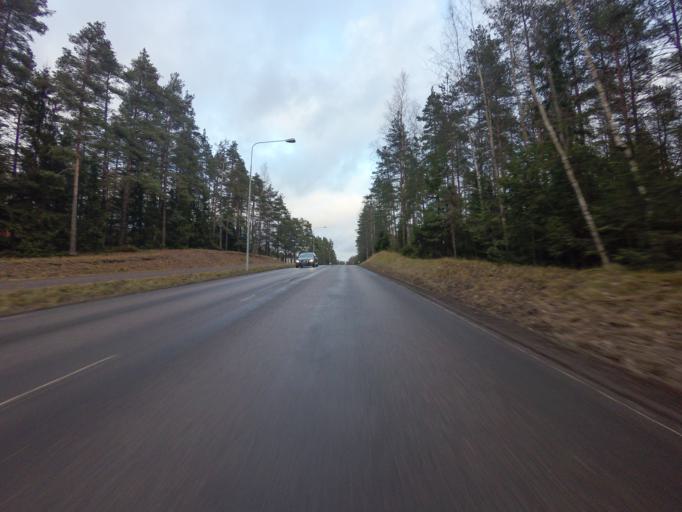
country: FI
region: Uusimaa
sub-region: Helsinki
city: Lohja
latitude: 60.2705
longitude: 24.1273
